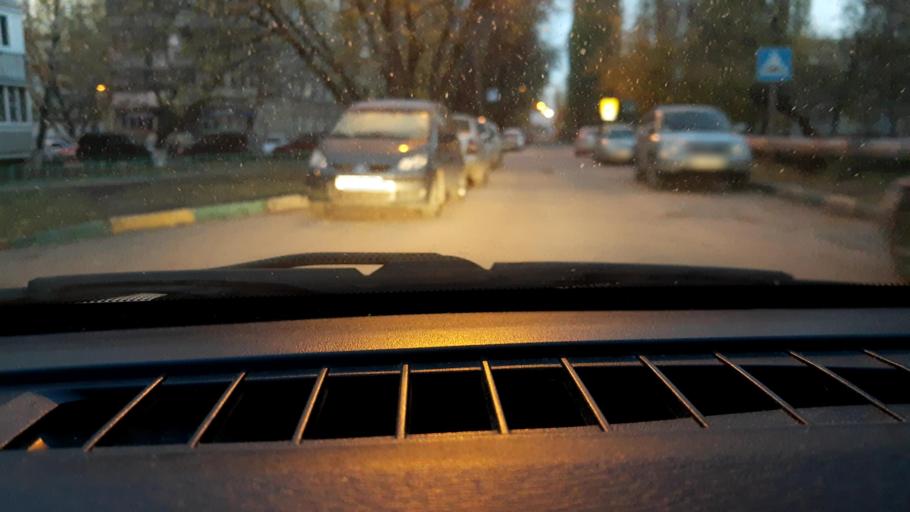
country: RU
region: Nizjnij Novgorod
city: Nizhniy Novgorod
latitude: 56.2861
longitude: 43.9482
